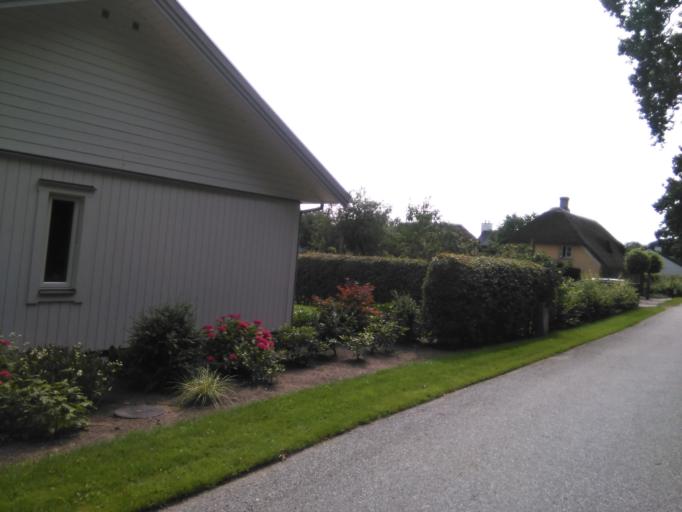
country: DK
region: Central Jutland
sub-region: Odder Kommune
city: Odder
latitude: 55.8816
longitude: 10.0551
